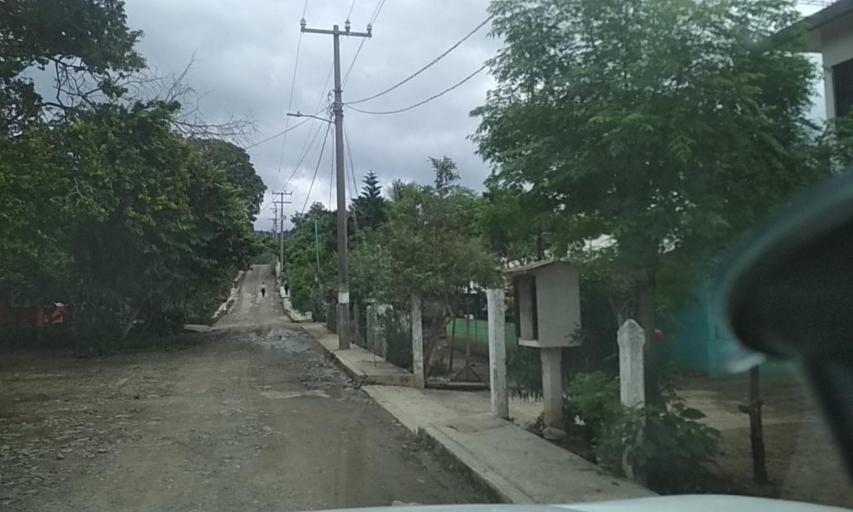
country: MX
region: Veracruz
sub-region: Papantla
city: Polutla
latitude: 20.5396
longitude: -97.2495
